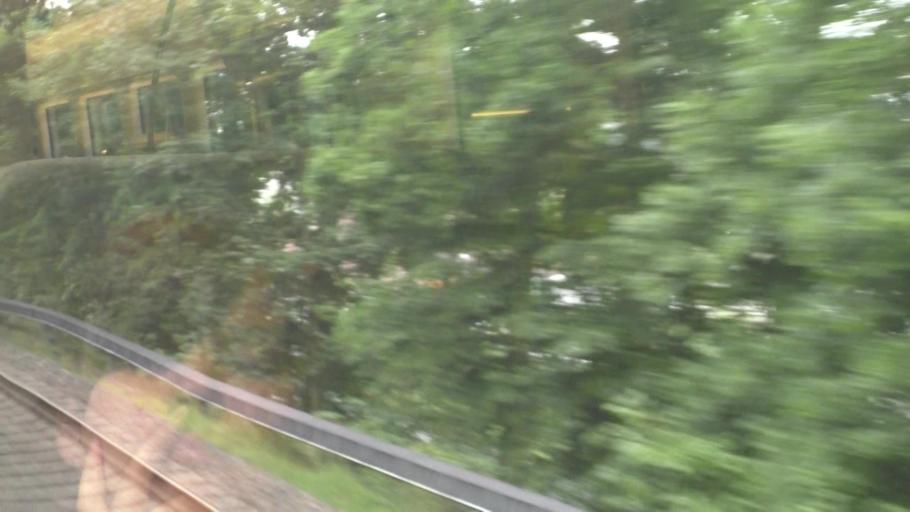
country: DE
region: Saxony
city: Bischofswerda
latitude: 51.1192
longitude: 14.1690
